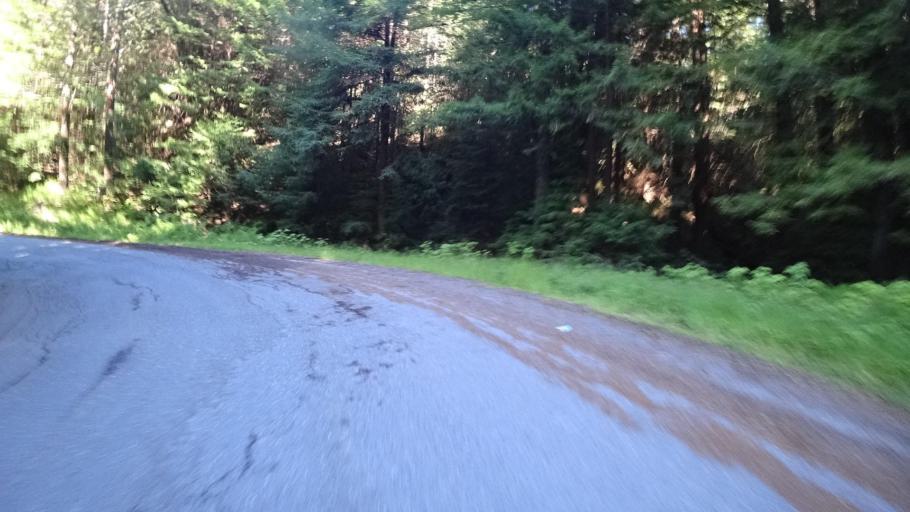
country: US
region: California
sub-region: Humboldt County
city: Rio Dell
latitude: 40.4606
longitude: -124.0005
